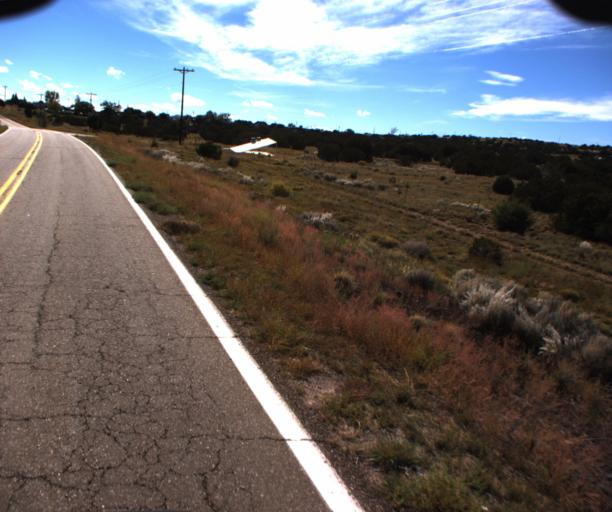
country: US
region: Arizona
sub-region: Apache County
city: Saint Johns
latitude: 34.4502
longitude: -109.6301
